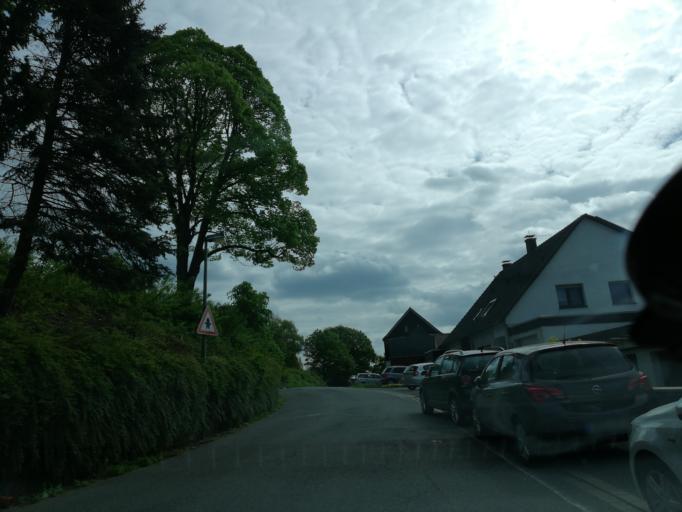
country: DE
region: North Rhine-Westphalia
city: Wetter (Ruhr)
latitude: 51.3802
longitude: 7.3434
